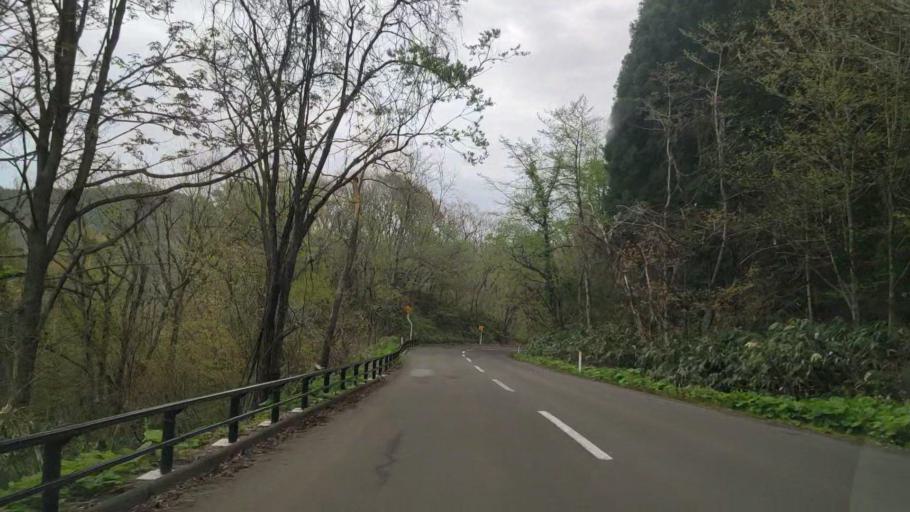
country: JP
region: Akita
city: Hanawa
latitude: 40.3740
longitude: 140.7899
